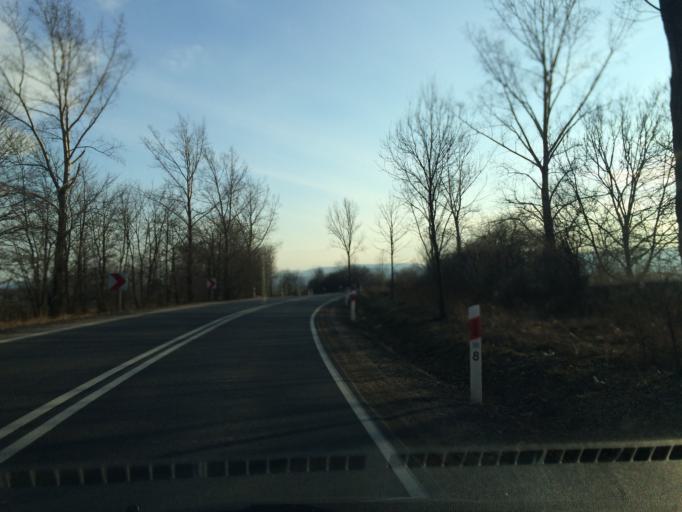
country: PL
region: Lower Silesian Voivodeship
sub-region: Powiat klodzki
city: Bystrzyca Klodzka
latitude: 50.2297
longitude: 16.6777
